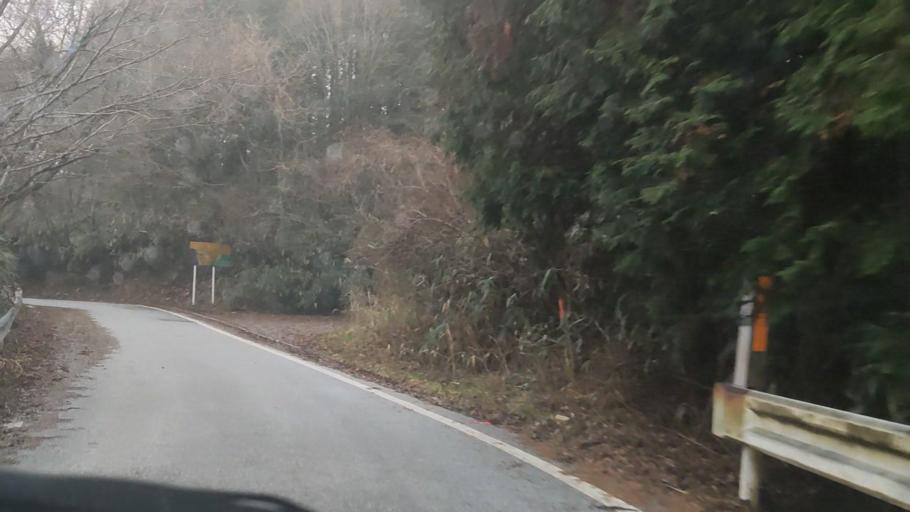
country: JP
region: Kumamoto
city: Matsubase
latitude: 32.5749
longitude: 130.9010
